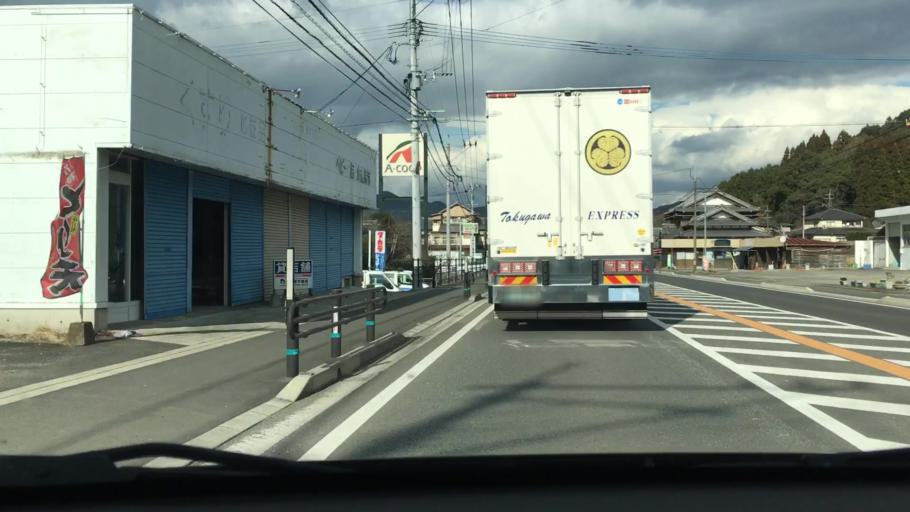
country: JP
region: Oita
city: Usuki
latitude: 33.0369
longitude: 131.6894
